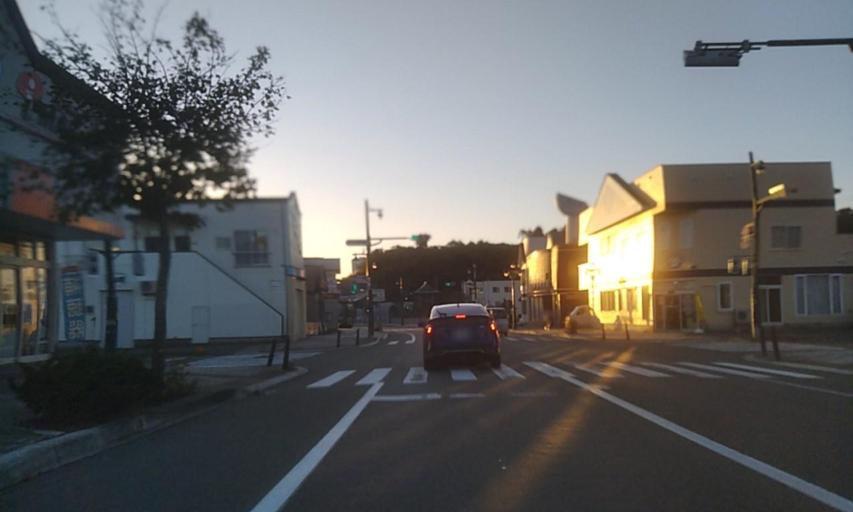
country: JP
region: Hokkaido
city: Shizunai-furukawacho
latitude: 42.1606
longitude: 142.7798
